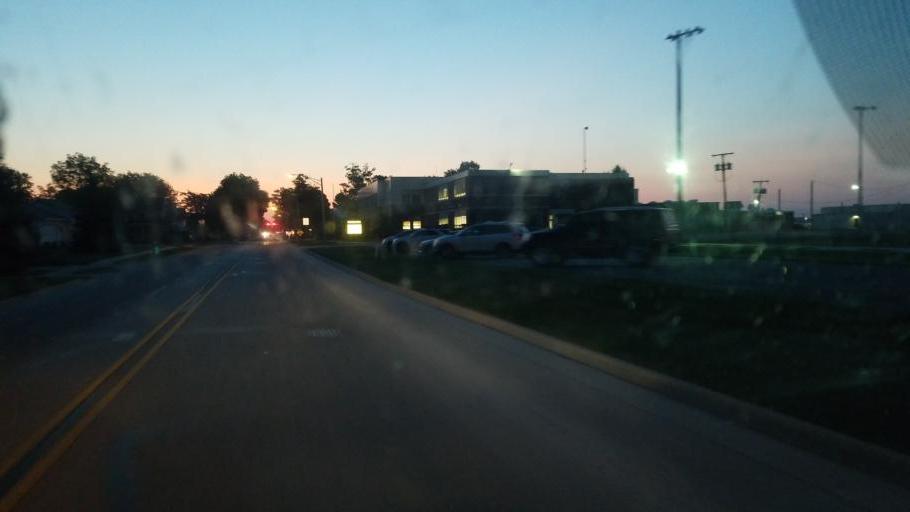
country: US
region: Indiana
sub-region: Elkhart County
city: Middlebury
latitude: 41.6763
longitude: -85.5851
